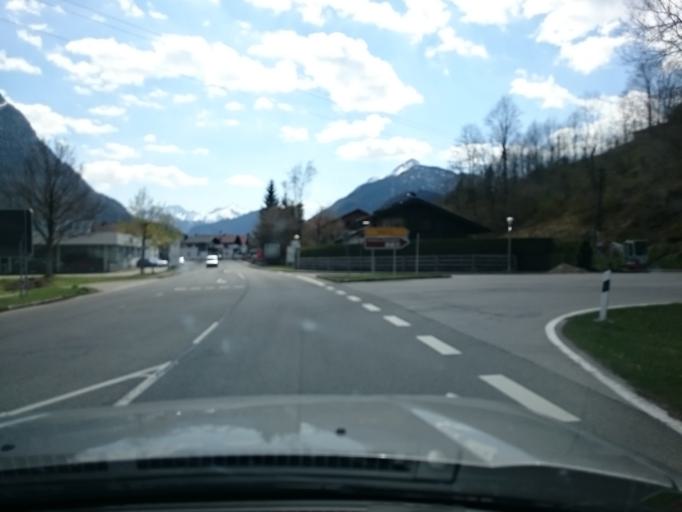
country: DE
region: Bavaria
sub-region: Upper Bavaria
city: Mittenwald
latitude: 47.4501
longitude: 11.2667
